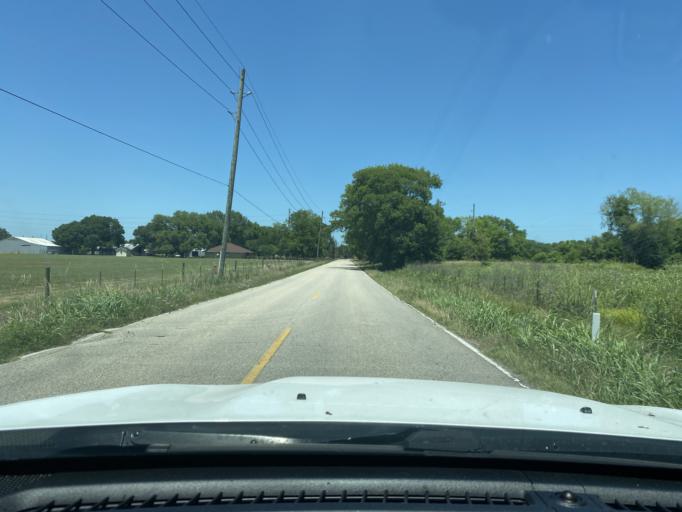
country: US
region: Texas
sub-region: Waller County
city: Waller
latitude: 30.0181
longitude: -95.8487
